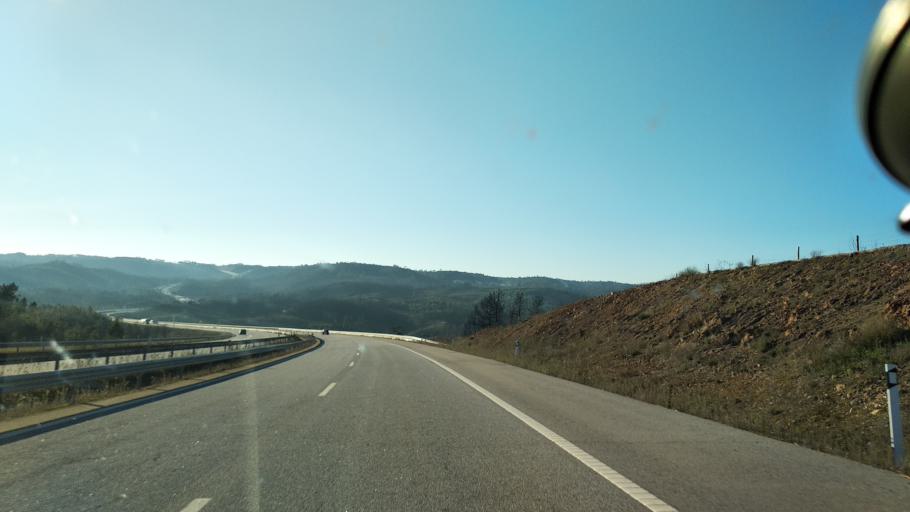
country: PT
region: Santarem
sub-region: Macao
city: Macao
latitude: 39.5256
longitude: -7.9684
